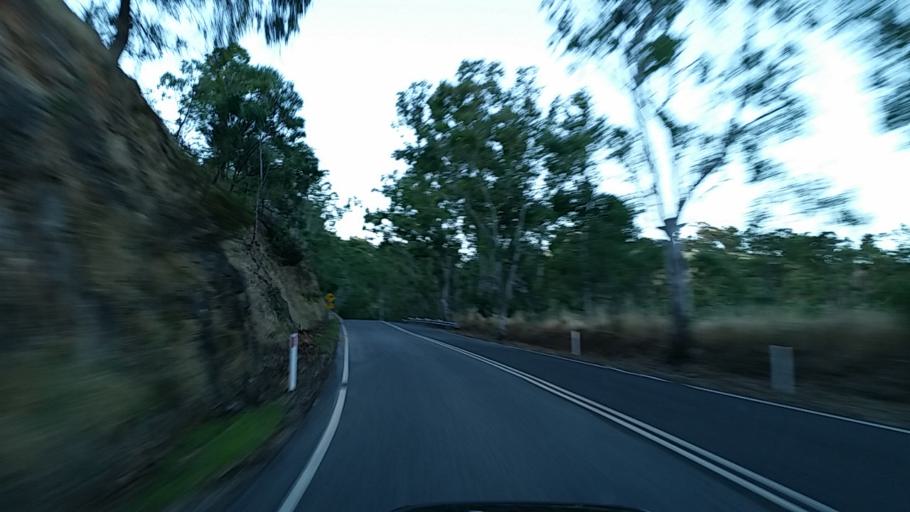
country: AU
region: South Australia
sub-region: Campbelltown
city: Athelstone
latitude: -34.8595
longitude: 138.7874
